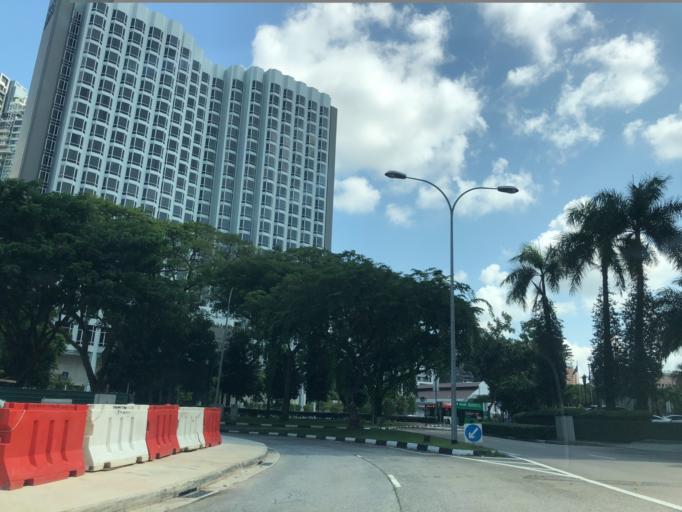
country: SG
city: Singapore
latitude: 1.2884
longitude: 103.8360
